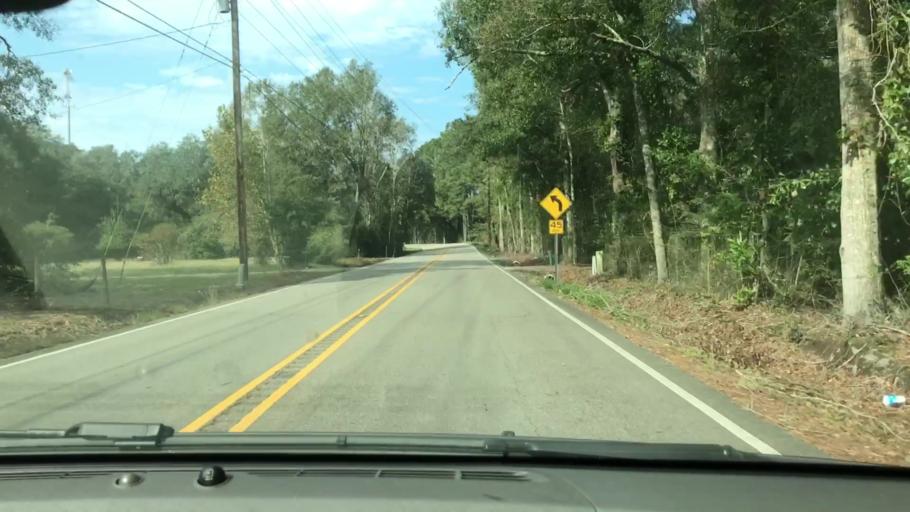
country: US
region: Louisiana
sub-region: Saint Tammany Parish
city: Abita Springs
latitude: 30.5336
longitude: -89.8838
